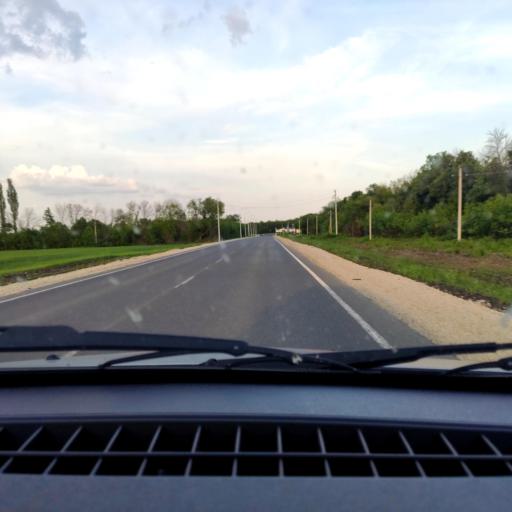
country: RU
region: Voronezj
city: Ramon'
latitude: 51.9192
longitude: 39.3148
